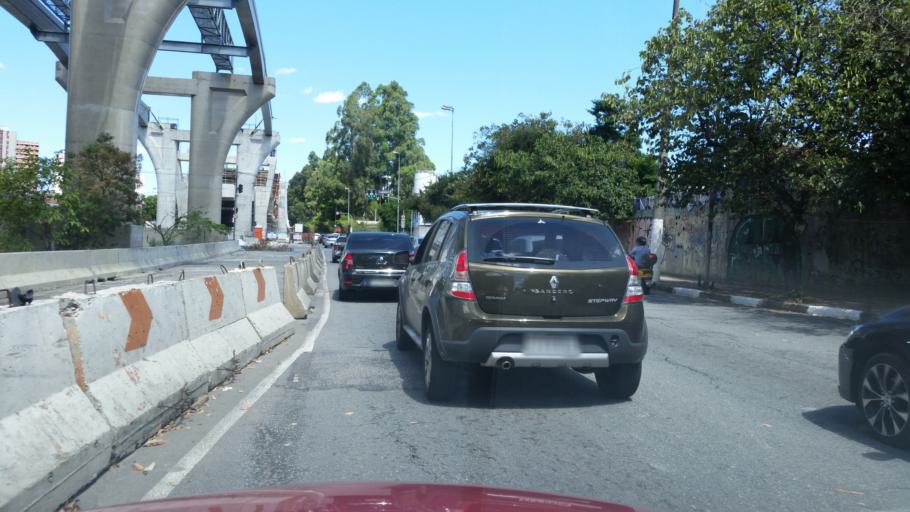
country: BR
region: Sao Paulo
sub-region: Diadema
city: Diadema
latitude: -23.6286
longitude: -46.6746
